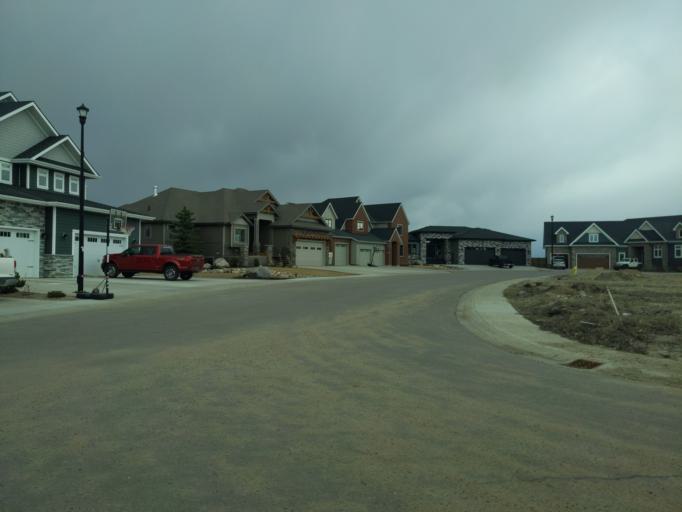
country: CA
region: Saskatchewan
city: Lloydminster
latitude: 53.2558
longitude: -110.0401
